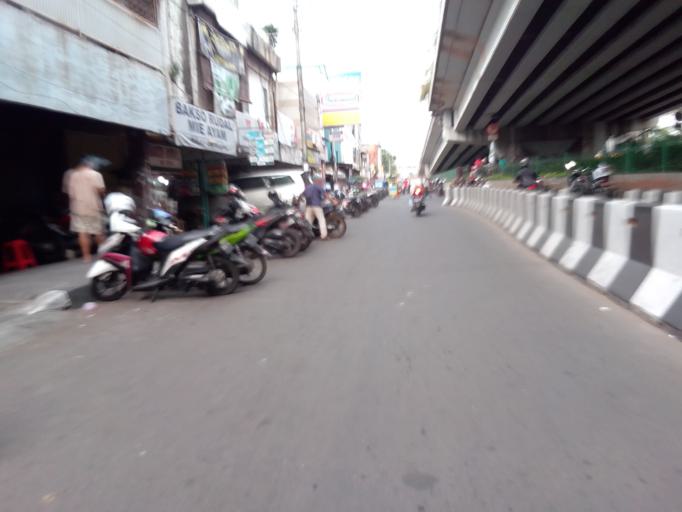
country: ID
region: Jakarta Raya
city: Jakarta
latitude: -6.1660
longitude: 106.8026
